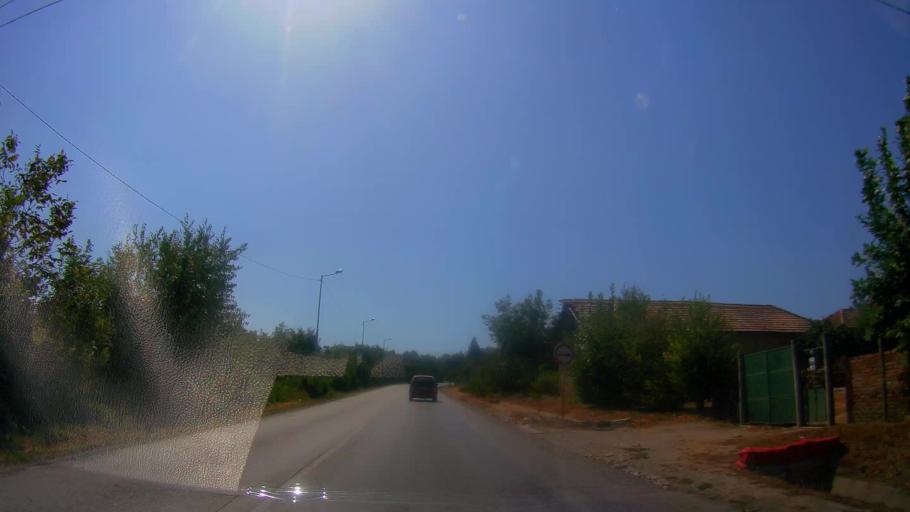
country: BG
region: Veliko Turnovo
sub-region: Obshtina Gorna Oryakhovitsa
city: Purvomaytsi
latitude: 43.1709
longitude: 25.6208
